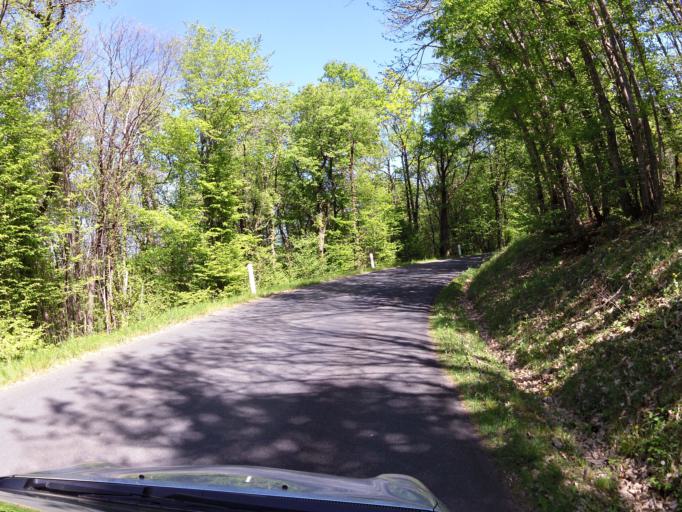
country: FR
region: Aquitaine
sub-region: Departement de la Dordogne
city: Sarlat-la-Caneda
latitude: 44.9237
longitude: 1.1566
